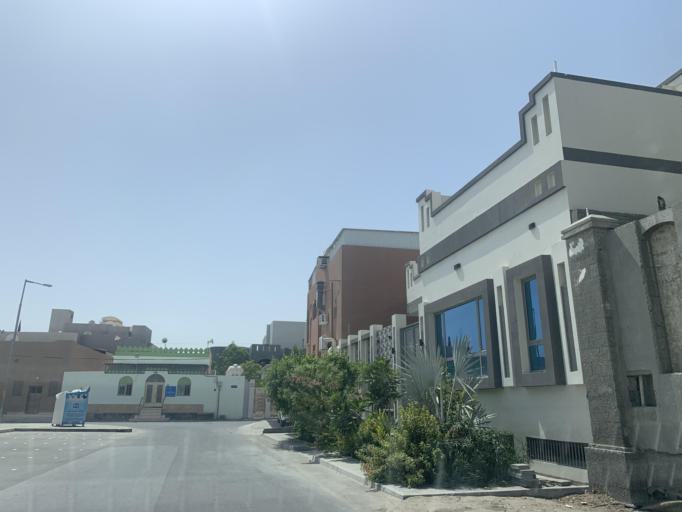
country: BH
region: Central Governorate
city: Madinat Hamad
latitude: 26.1486
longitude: 50.4973
